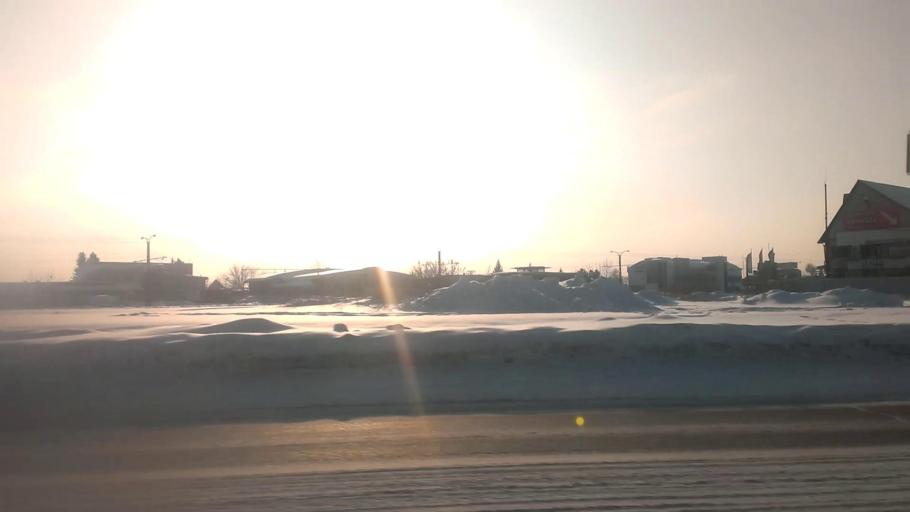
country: RU
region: Altai Krai
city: Novosilikatnyy
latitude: 53.3304
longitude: 83.6616
